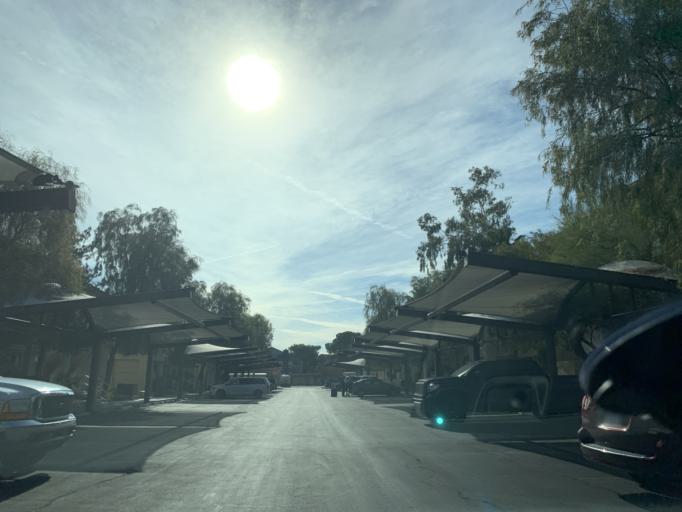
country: US
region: Nevada
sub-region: Clark County
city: Spring Valley
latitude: 36.0998
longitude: -115.2139
